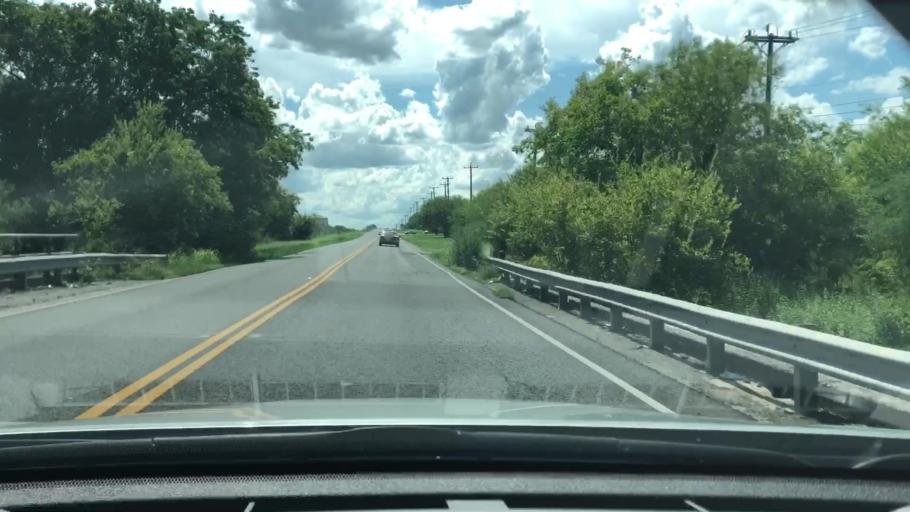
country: US
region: Texas
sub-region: Bexar County
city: Windcrest
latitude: 29.4952
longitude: -98.3522
